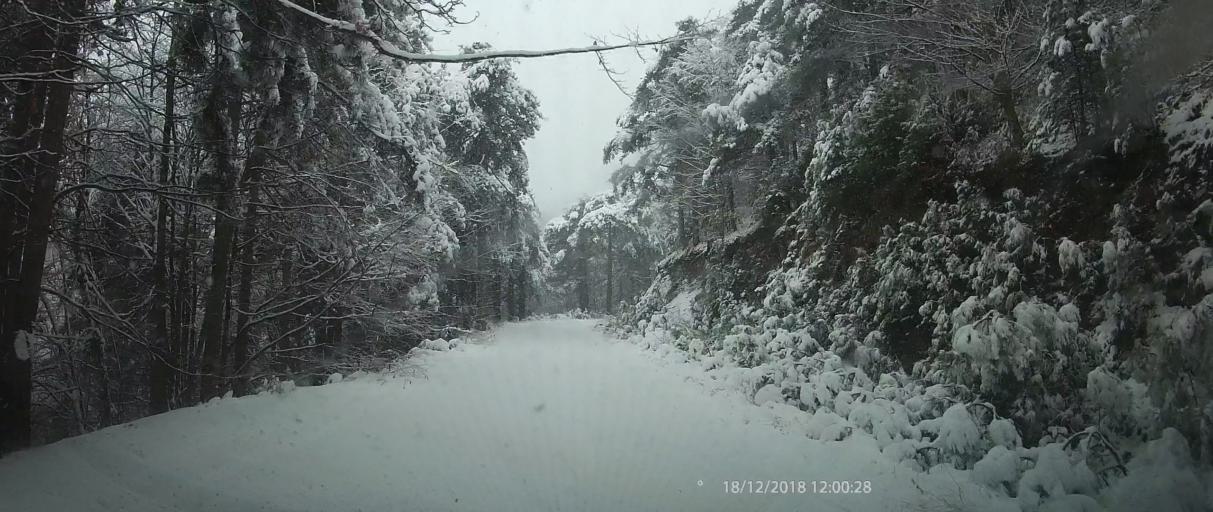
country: GR
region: Central Macedonia
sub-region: Nomos Pierias
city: Litochoro
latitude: 40.1105
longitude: 22.4639
